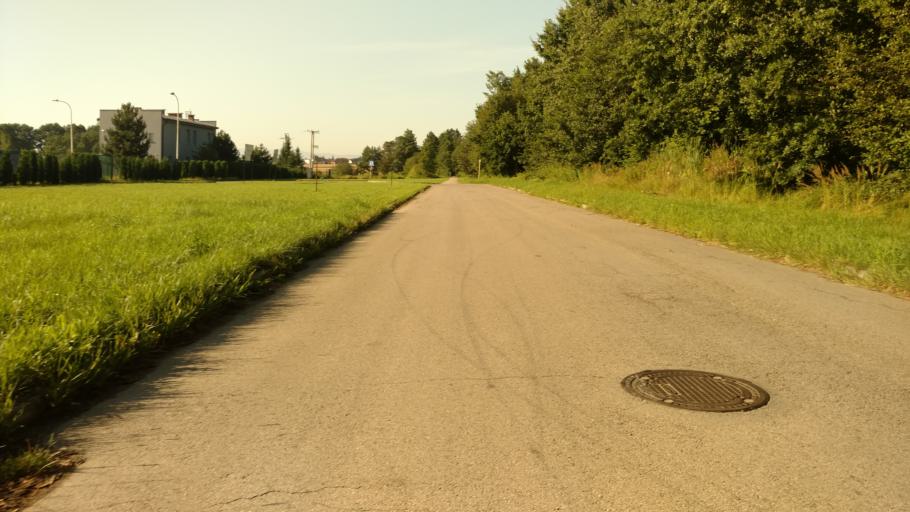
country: PL
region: Silesian Voivodeship
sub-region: Powiat pszczynski
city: Pszczyna
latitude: 49.9842
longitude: 18.9699
